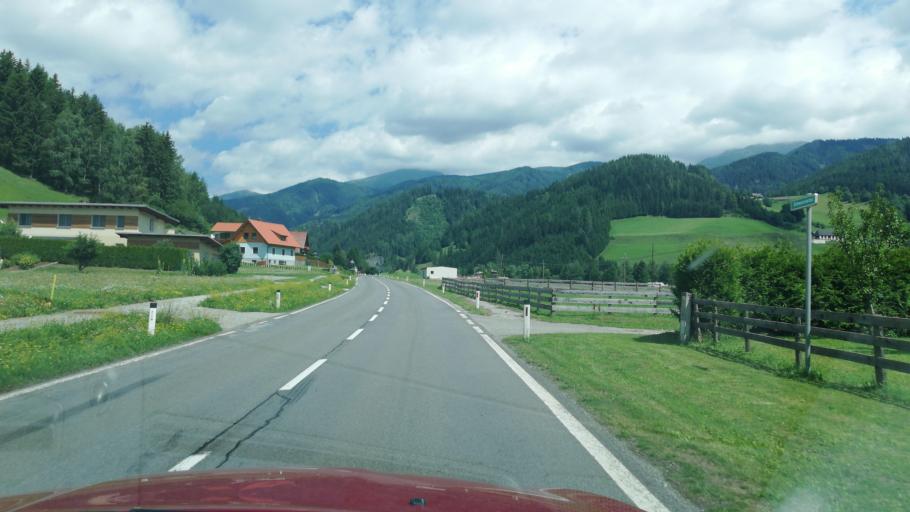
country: AT
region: Styria
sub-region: Politischer Bezirk Murtal
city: Oberzeiring
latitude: 47.2893
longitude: 14.4851
